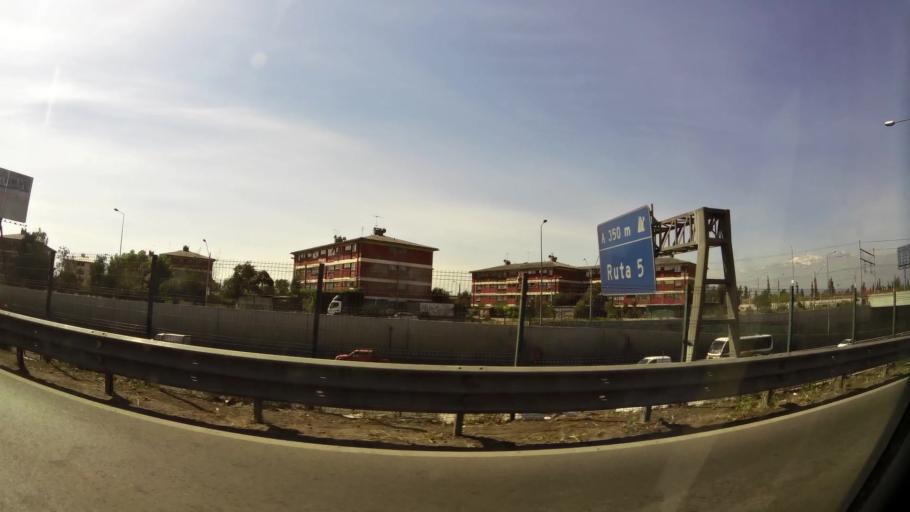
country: CL
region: Santiago Metropolitan
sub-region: Provincia de Maipo
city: San Bernardo
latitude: -33.5282
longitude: -70.6900
